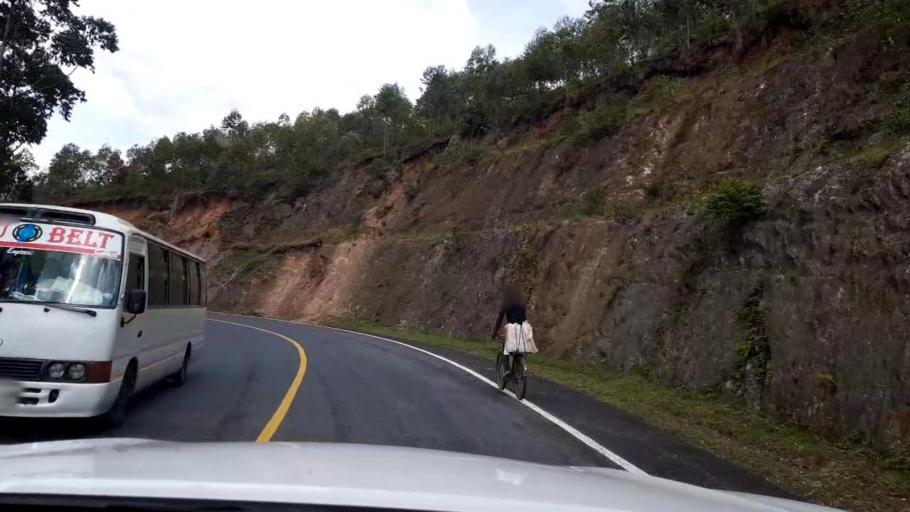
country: RW
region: Southern Province
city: Gitarama
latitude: -2.0277
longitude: 29.7171
